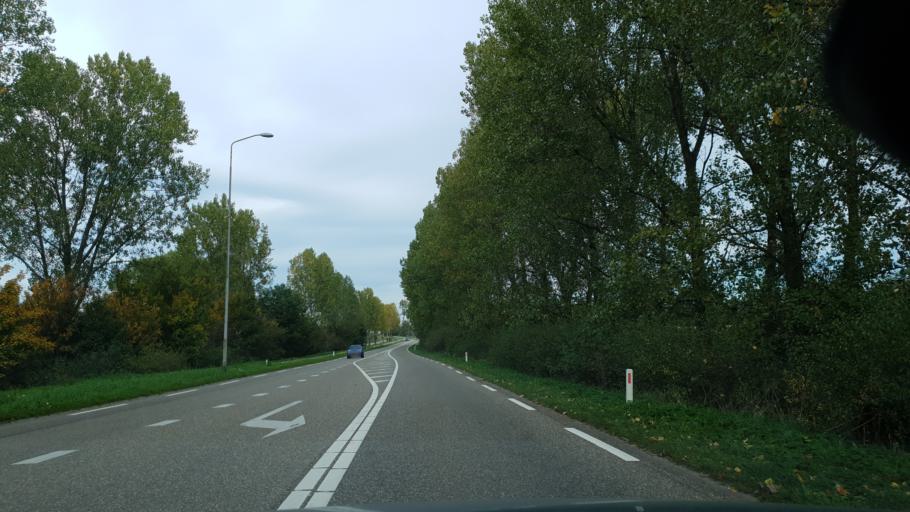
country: NL
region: Gelderland
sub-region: Gemeente Wijchen
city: Bergharen
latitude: 51.8739
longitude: 5.6604
